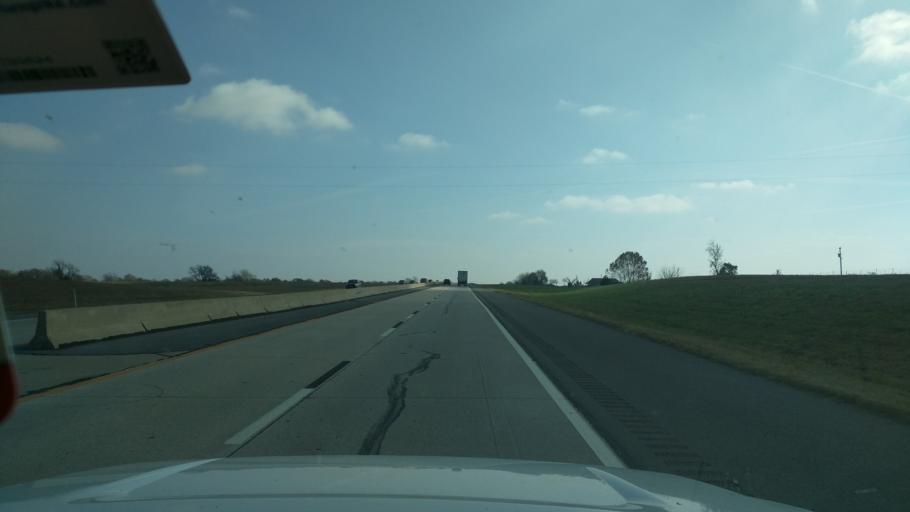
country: US
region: Oklahoma
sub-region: Wagoner County
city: Wagoner
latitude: 35.8853
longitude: -95.4926
